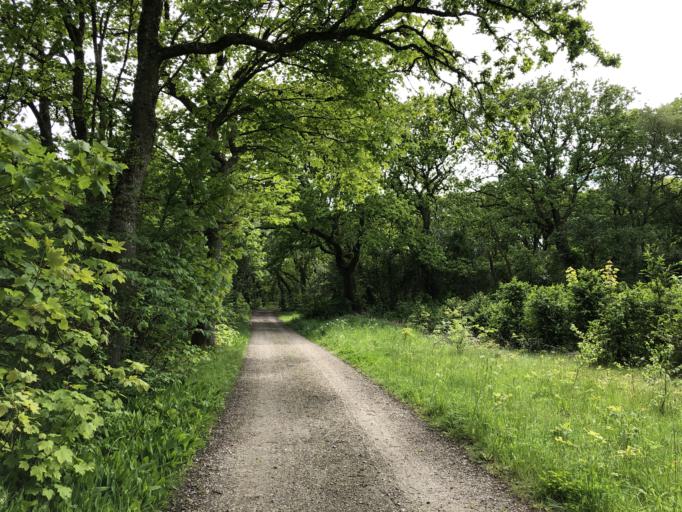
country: DK
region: Central Jutland
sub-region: Holstebro Kommune
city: Ulfborg
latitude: 56.2809
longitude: 8.1710
